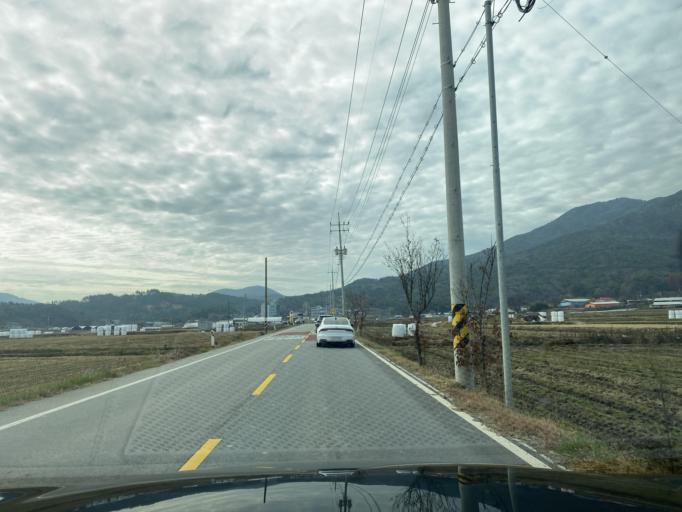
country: KR
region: Chungcheongnam-do
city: Hongsung
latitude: 36.6804
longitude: 126.6466
